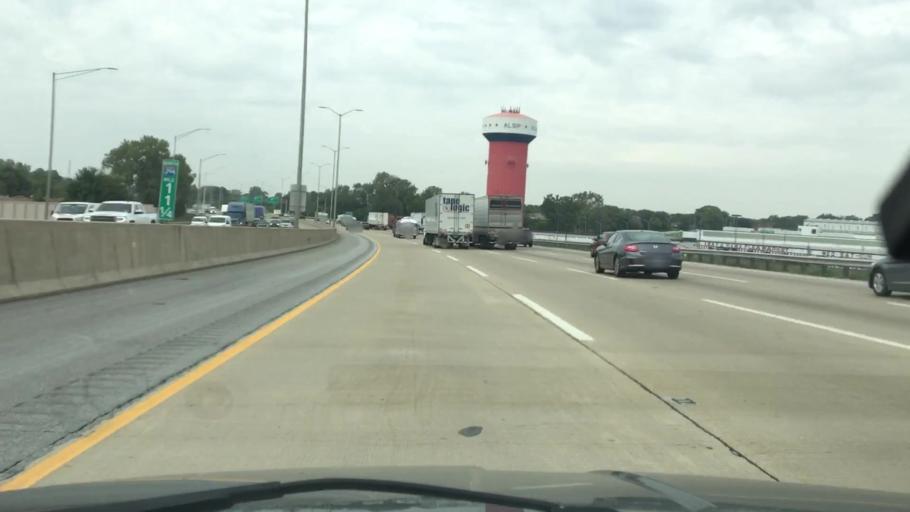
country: US
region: Illinois
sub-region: Cook County
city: Alsip
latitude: 41.6557
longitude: -87.7272
